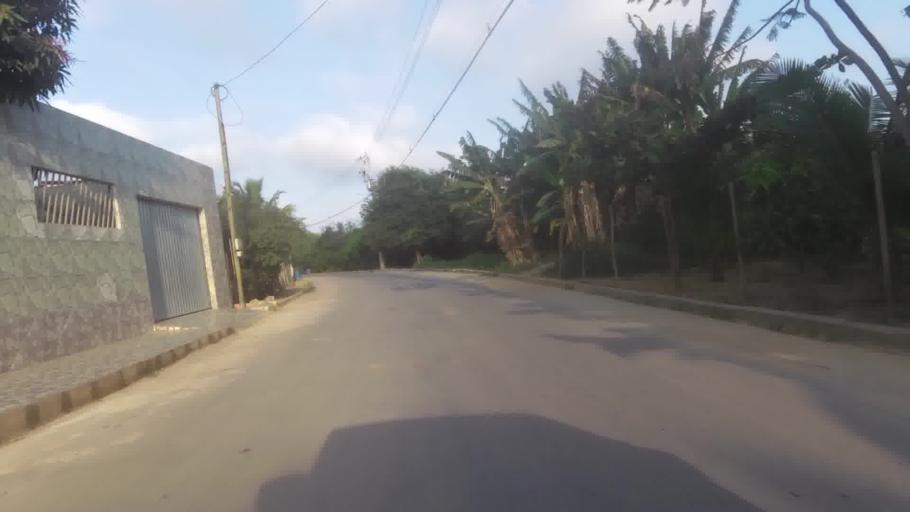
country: BR
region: Espirito Santo
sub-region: Itapemirim
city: Itapemirim
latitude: -21.0171
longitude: -40.8291
